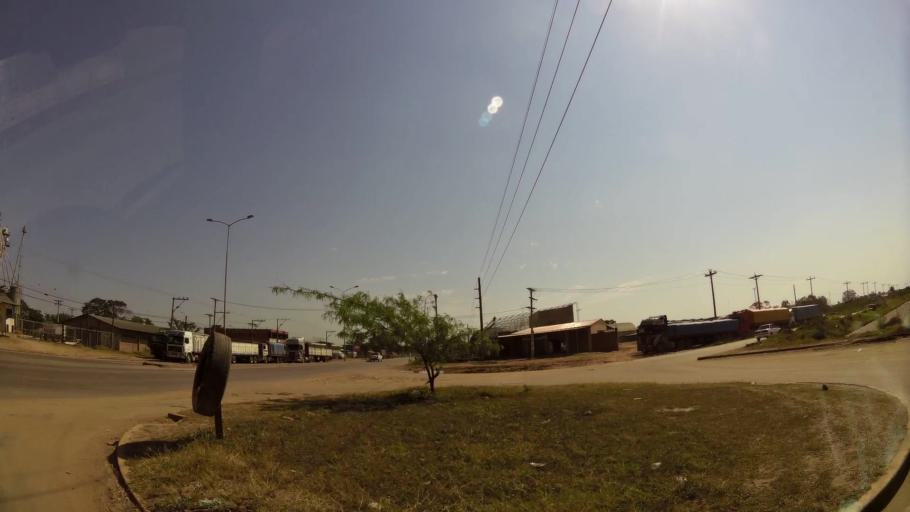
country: BO
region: Santa Cruz
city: Cotoca
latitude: -17.7648
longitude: -63.0890
